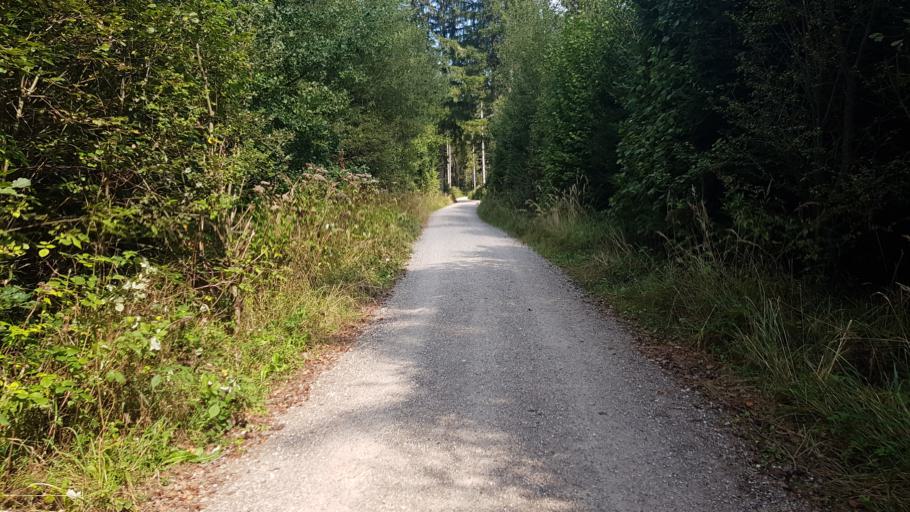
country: DE
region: Bavaria
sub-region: Upper Bavaria
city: Gilching
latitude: 48.0851
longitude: 11.3024
